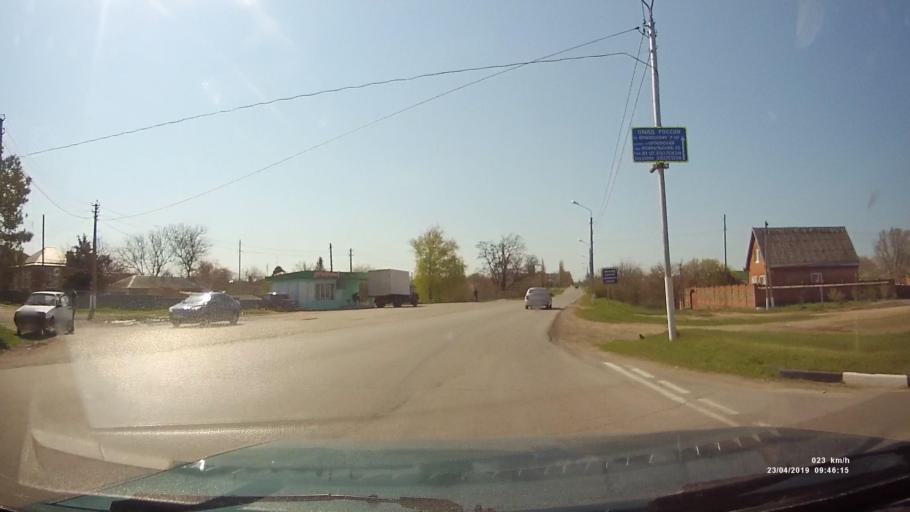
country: RU
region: Rostov
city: Orlovskiy
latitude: 46.8833
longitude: 42.0383
